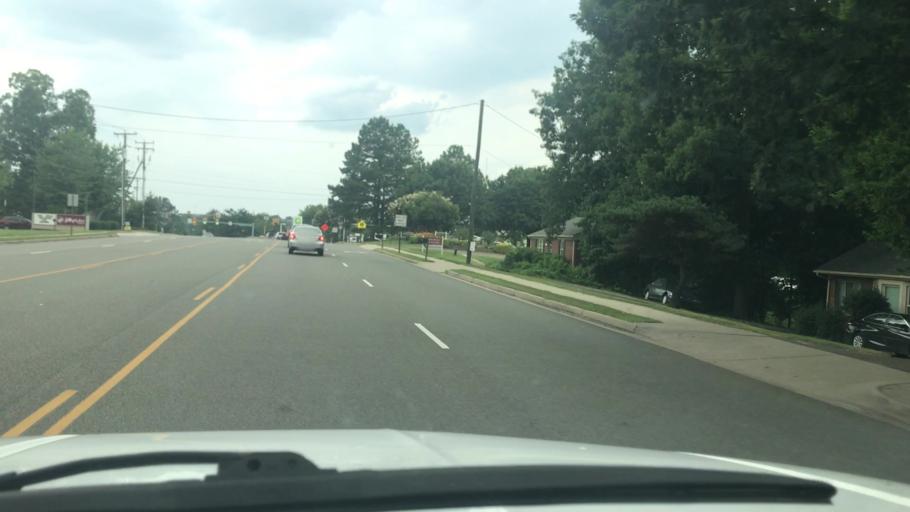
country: US
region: Virginia
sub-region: Henrico County
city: Tuckahoe
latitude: 37.6070
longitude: -77.5764
